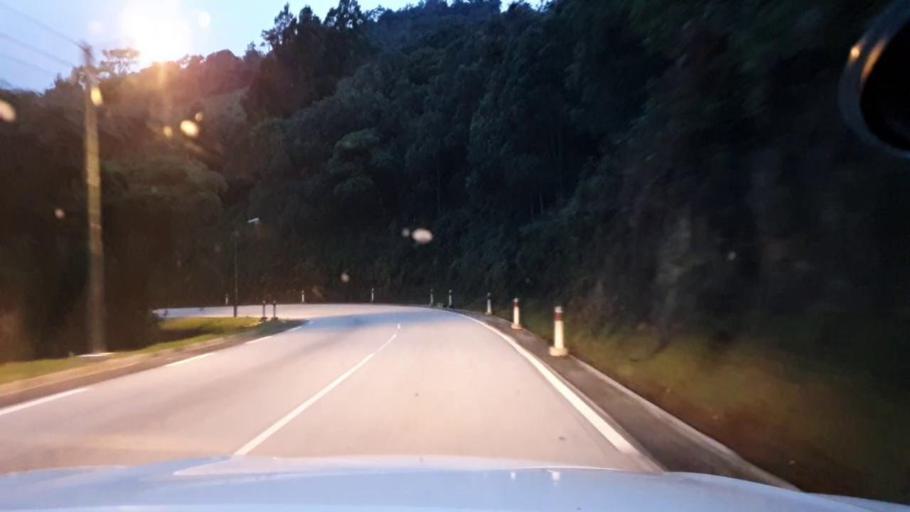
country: RW
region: Southern Province
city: Nzega
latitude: -2.5267
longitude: 29.3797
